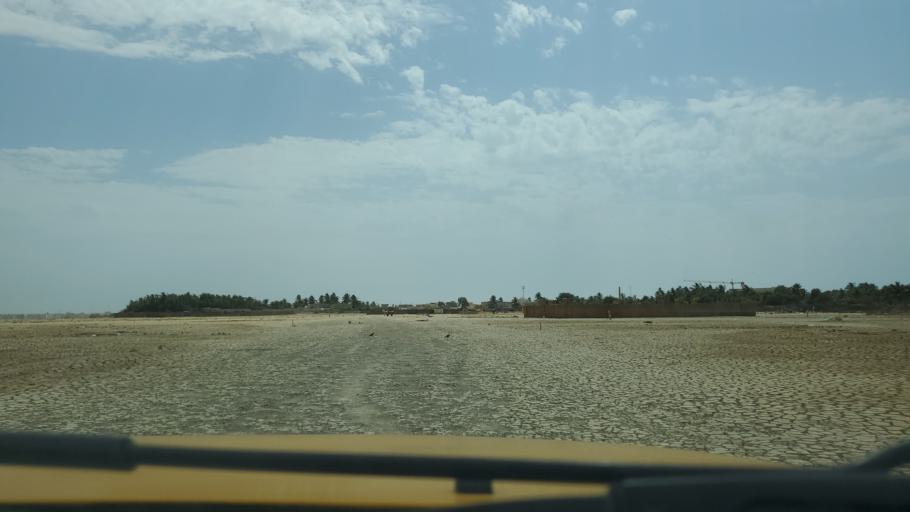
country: SN
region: Saint-Louis
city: Saint-Louis
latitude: 16.0271
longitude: -16.4686
